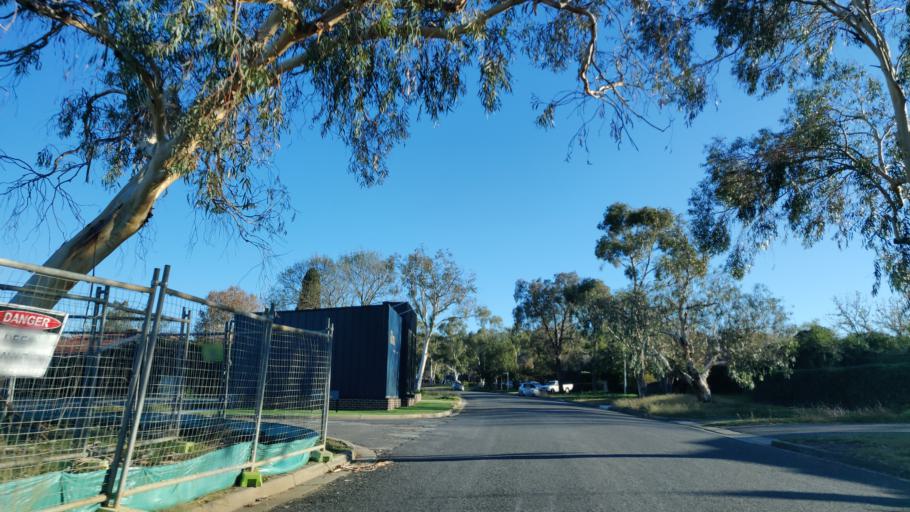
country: AU
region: Australian Capital Territory
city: Forrest
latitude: -35.3321
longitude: 149.1444
